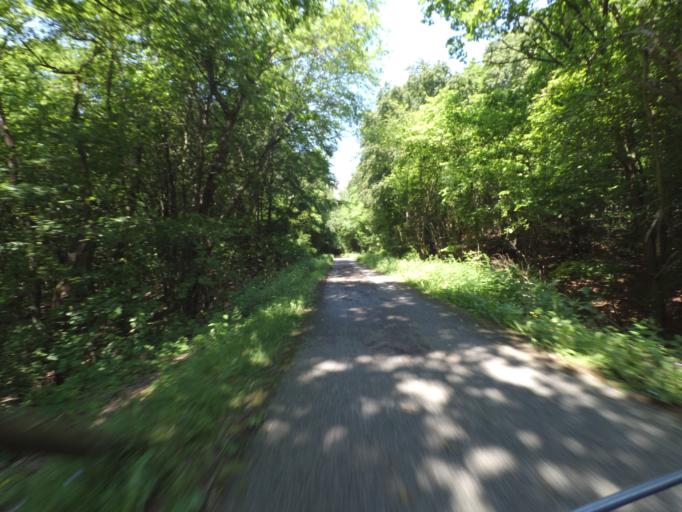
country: DE
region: Rheinland-Pfalz
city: Leiningen
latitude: 50.1249
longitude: 7.5663
